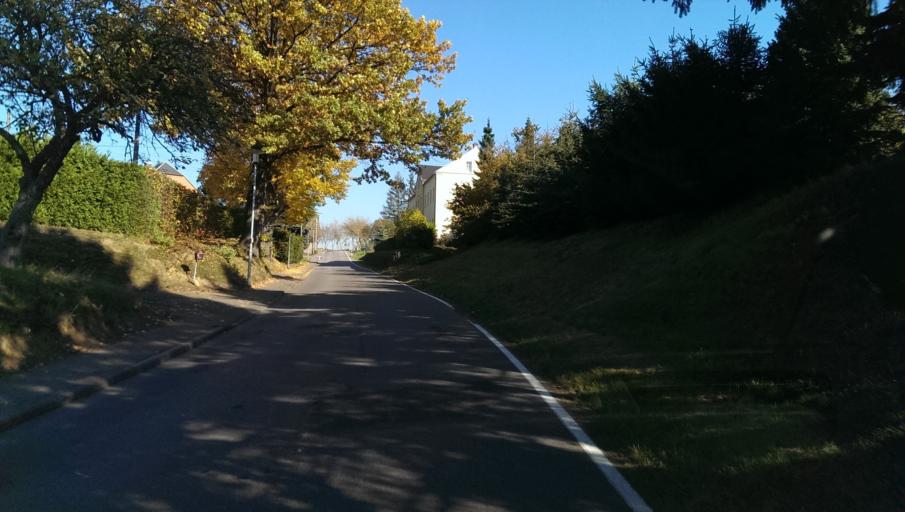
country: DE
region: Saxony
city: Waldheim
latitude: 51.0829
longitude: 13.0354
